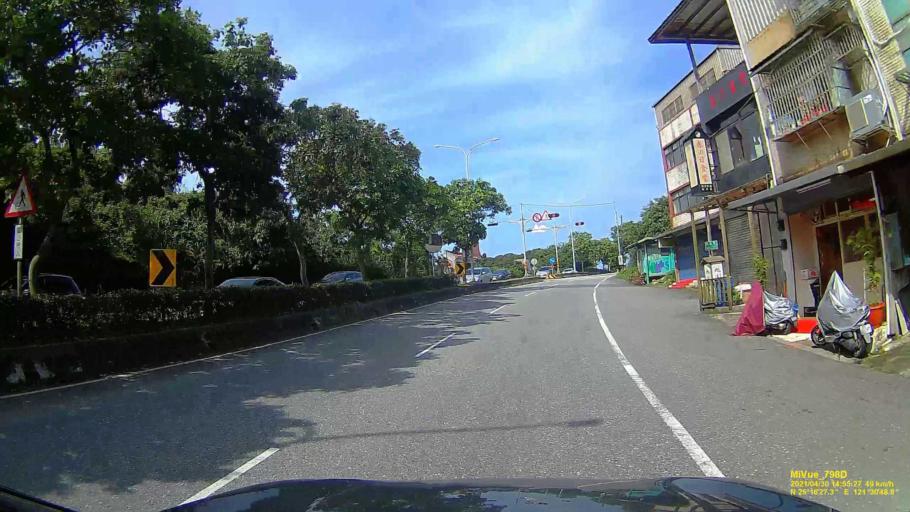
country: TW
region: Taipei
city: Taipei
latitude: 25.2745
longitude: 121.5139
